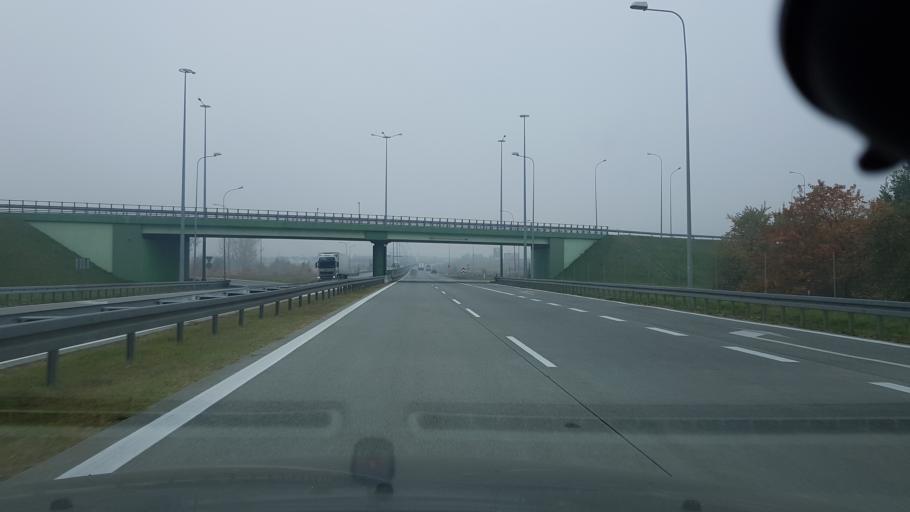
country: PL
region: Lodz Voivodeship
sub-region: Powiat rawski
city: Rawa Mazowiecka
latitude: 51.7741
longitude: 20.2744
